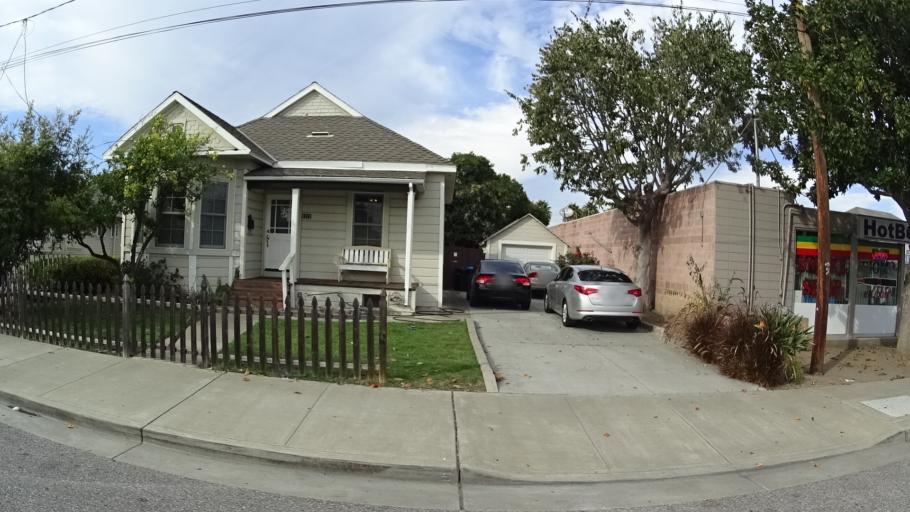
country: US
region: California
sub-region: Santa Clara County
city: Santa Clara
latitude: 37.3538
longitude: -121.9492
